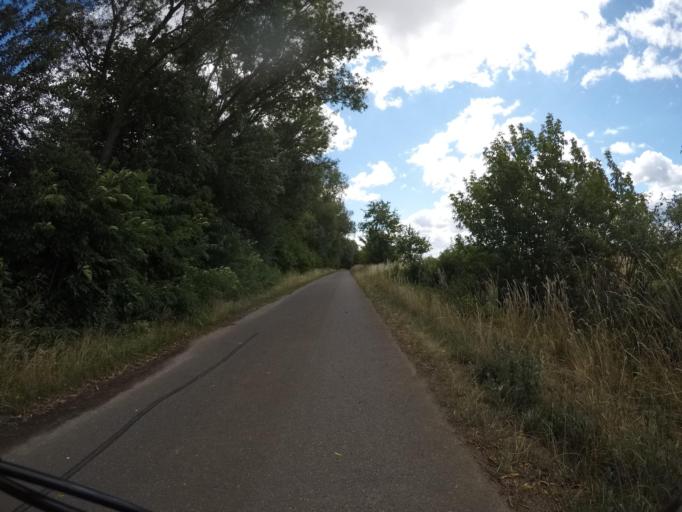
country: DE
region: Lower Saxony
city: Hitzacker
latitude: 53.1991
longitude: 11.0194
